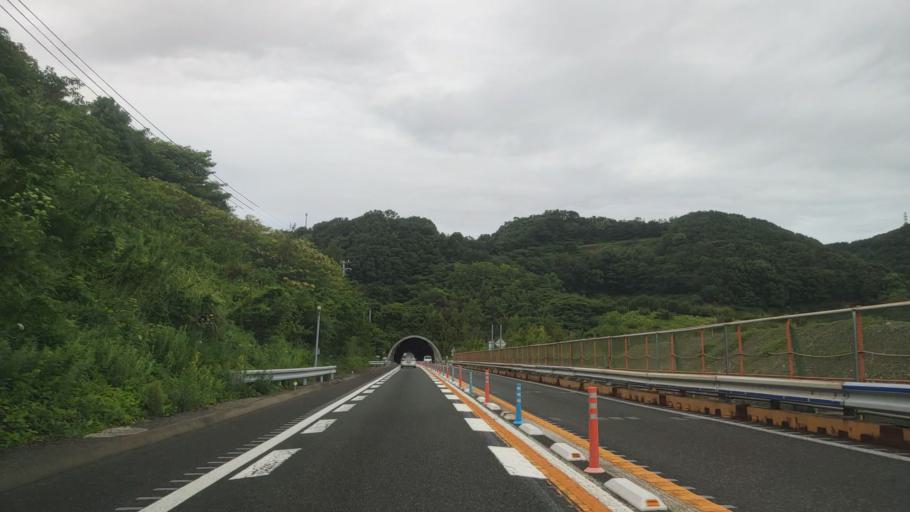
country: JP
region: Wakayama
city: Tanabe
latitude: 33.7845
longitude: 135.3132
